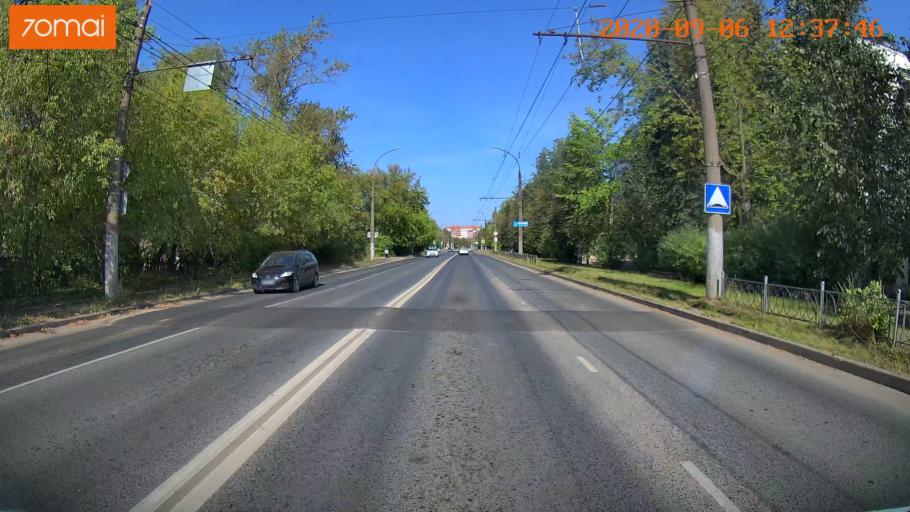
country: RU
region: Ivanovo
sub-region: Gorod Ivanovo
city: Ivanovo
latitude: 57.0287
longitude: 40.9803
